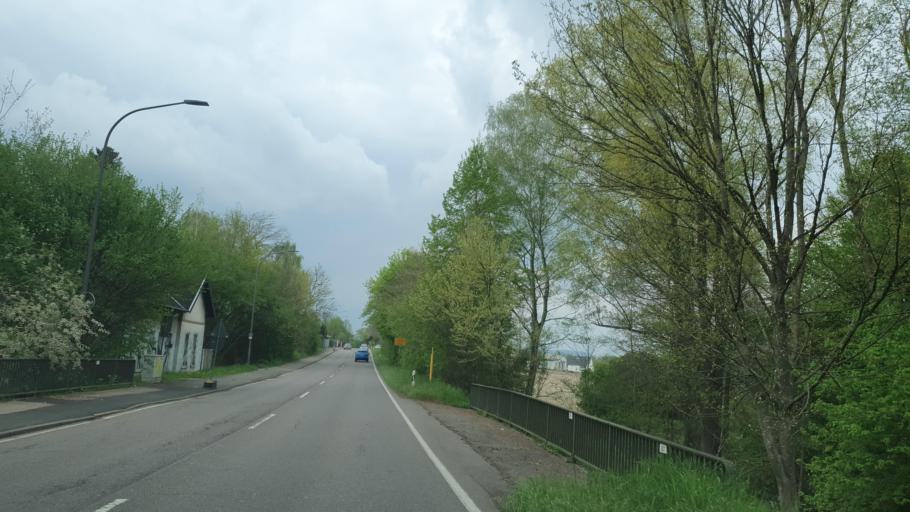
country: DE
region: Saarland
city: Saarlouis
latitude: 49.2978
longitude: 6.7376
